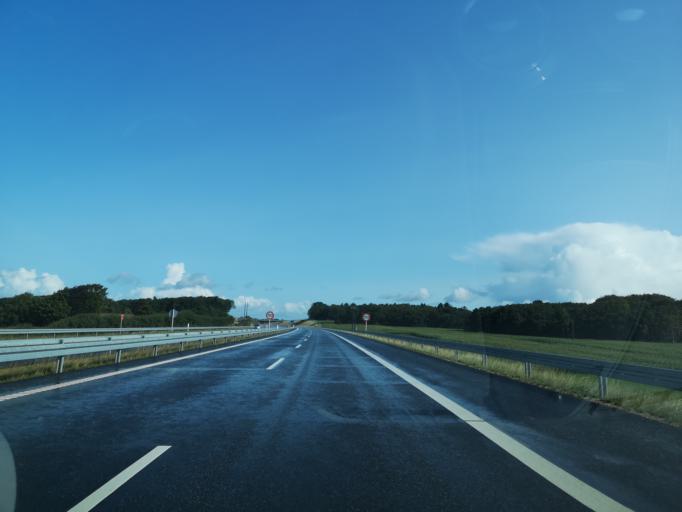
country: DK
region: Central Jutland
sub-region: Herning Kommune
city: Snejbjerg
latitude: 56.1678
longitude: 8.8891
